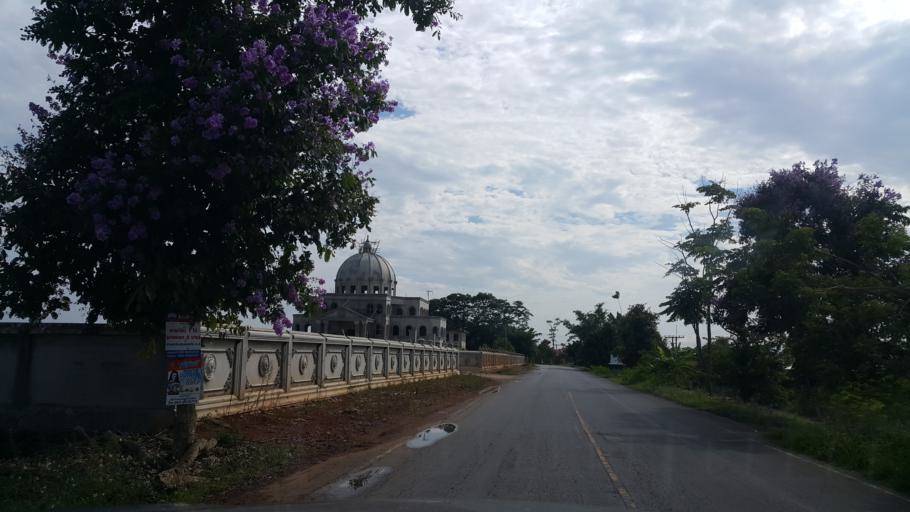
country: TH
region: Chiang Rai
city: Wiang Chai
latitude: 19.9550
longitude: 99.9340
